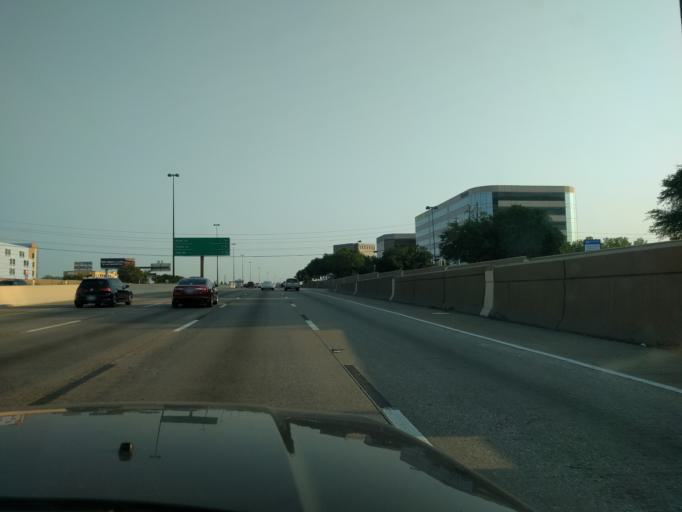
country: US
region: Texas
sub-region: Dallas County
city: University Park
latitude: 32.8832
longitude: -96.7700
